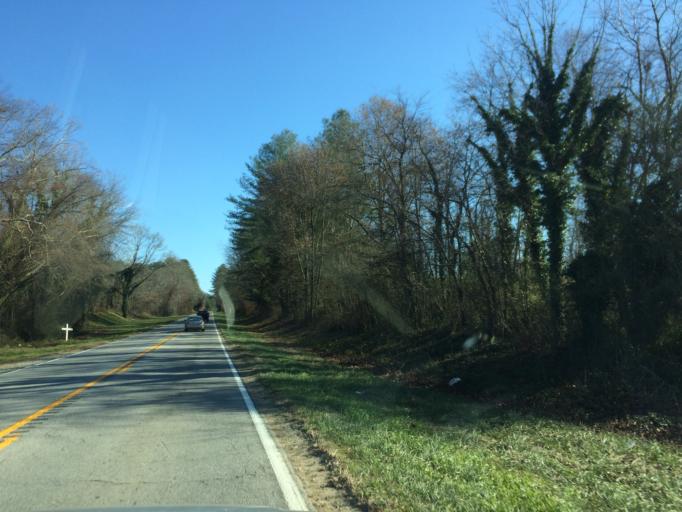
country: US
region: North Carolina
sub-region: Henderson County
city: Horse Shoe
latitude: 35.3711
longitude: -82.5317
